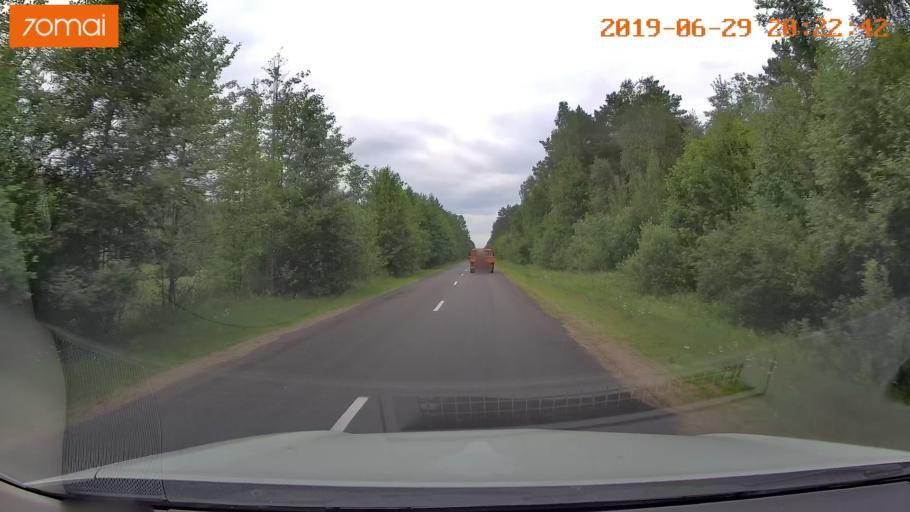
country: BY
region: Brest
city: Asnyezhytsy
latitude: 52.4353
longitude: 26.2562
